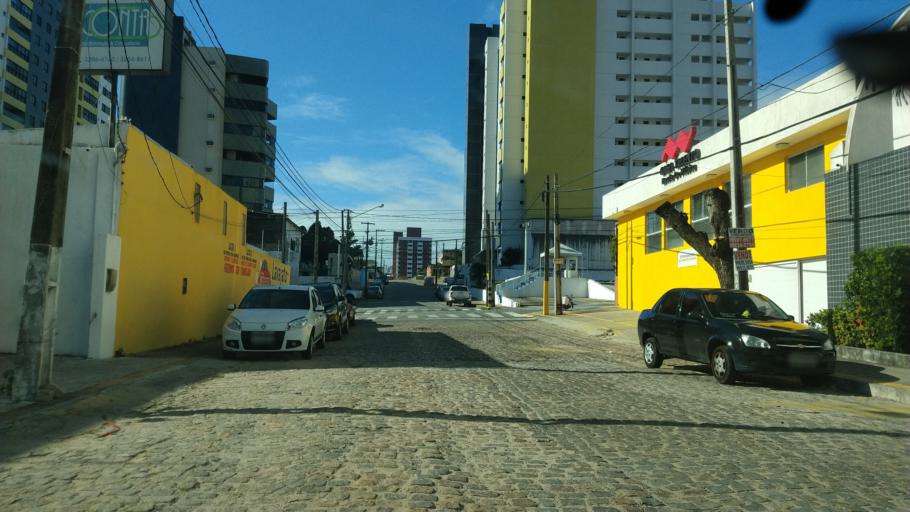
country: BR
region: Rio Grande do Norte
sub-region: Natal
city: Natal
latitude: -5.8200
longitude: -35.2067
